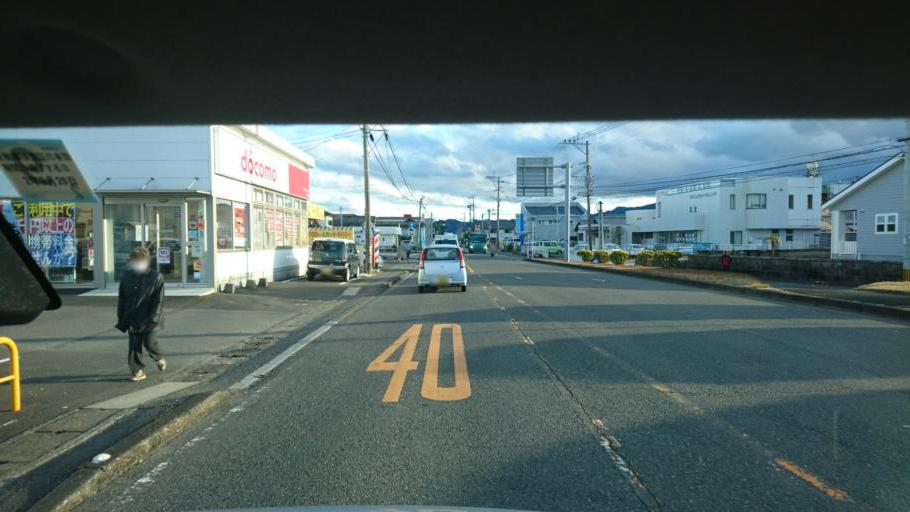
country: JP
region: Miyazaki
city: Miyazaki-shi
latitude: 31.8667
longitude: 131.4319
